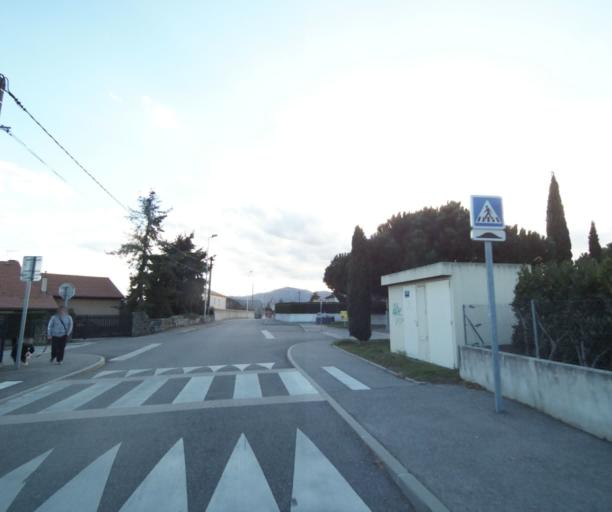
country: FR
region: Rhone-Alpes
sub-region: Departement de l'Ardeche
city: Davezieux
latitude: 45.2502
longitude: 4.6993
